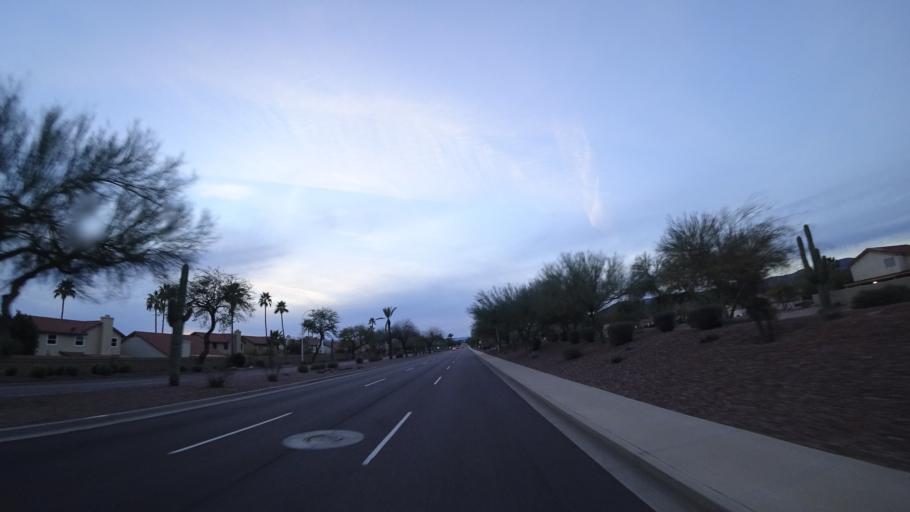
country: US
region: Arizona
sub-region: Maricopa County
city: Guadalupe
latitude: 33.3053
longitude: -112.0030
